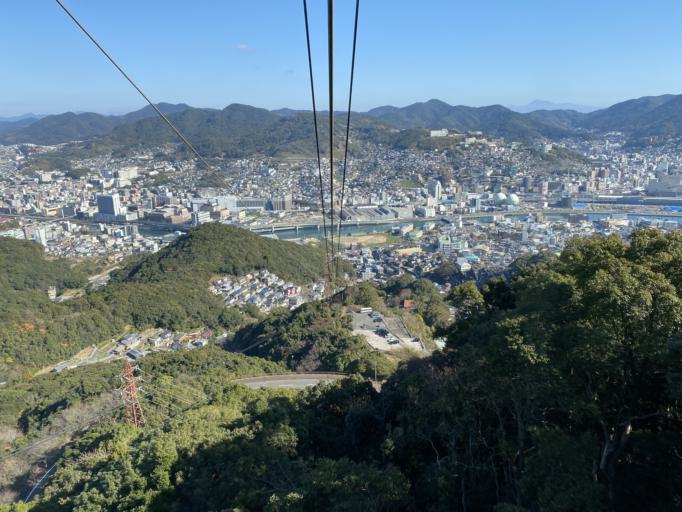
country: JP
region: Nagasaki
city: Nagasaki-shi
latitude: 32.7549
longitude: 129.8510
